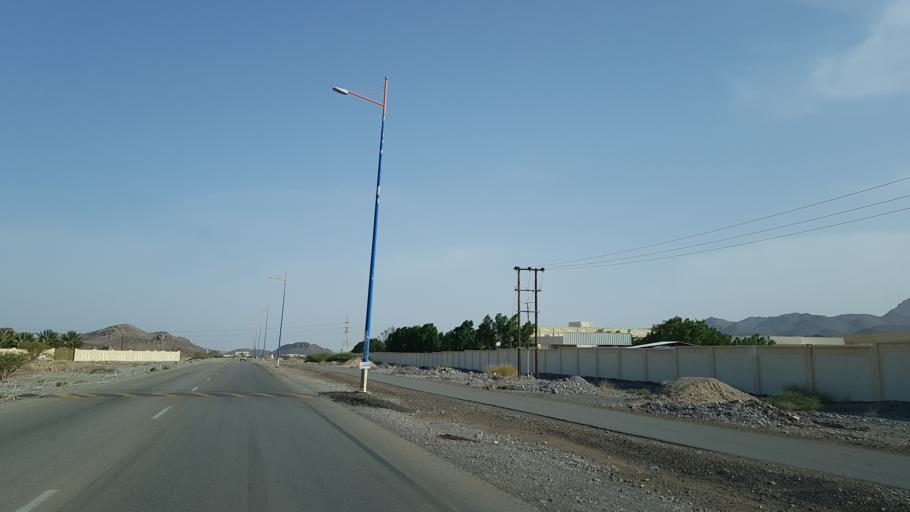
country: OM
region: Muhafazat ad Dakhiliyah
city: Izki
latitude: 22.9126
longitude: 57.6742
